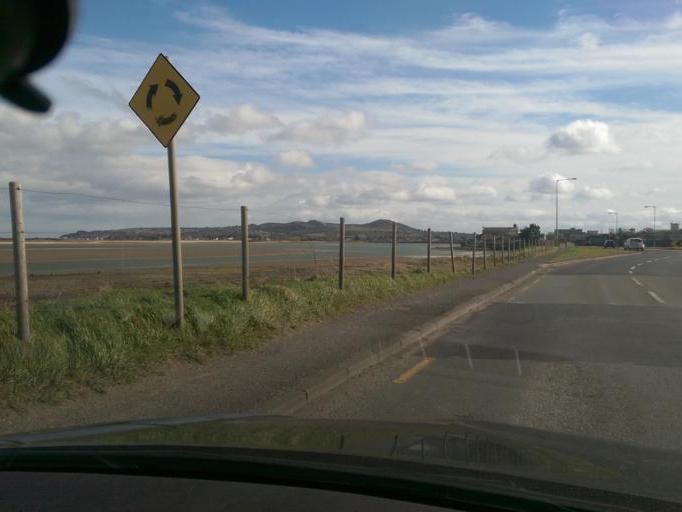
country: IE
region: Leinster
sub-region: Fingal County
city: Baldoyle
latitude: 53.4029
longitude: -6.1314
